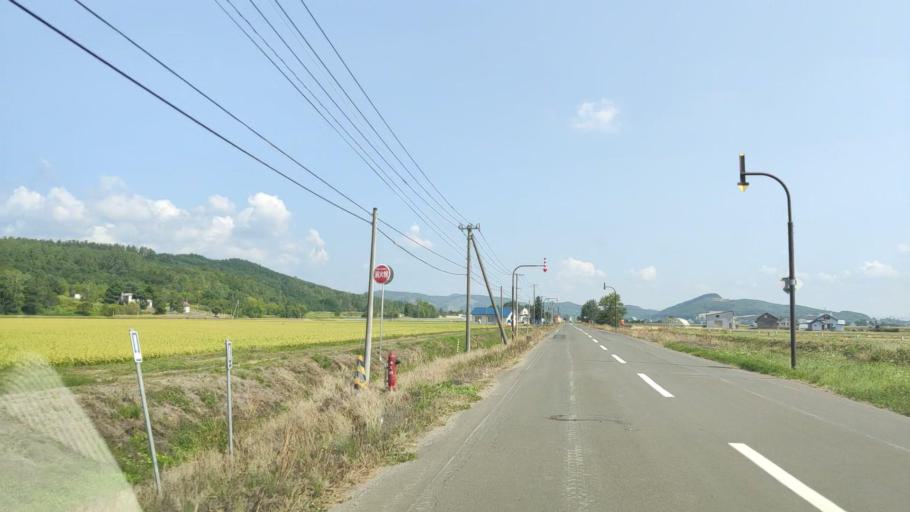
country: JP
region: Hokkaido
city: Shimo-furano
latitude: 43.3765
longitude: 142.3897
